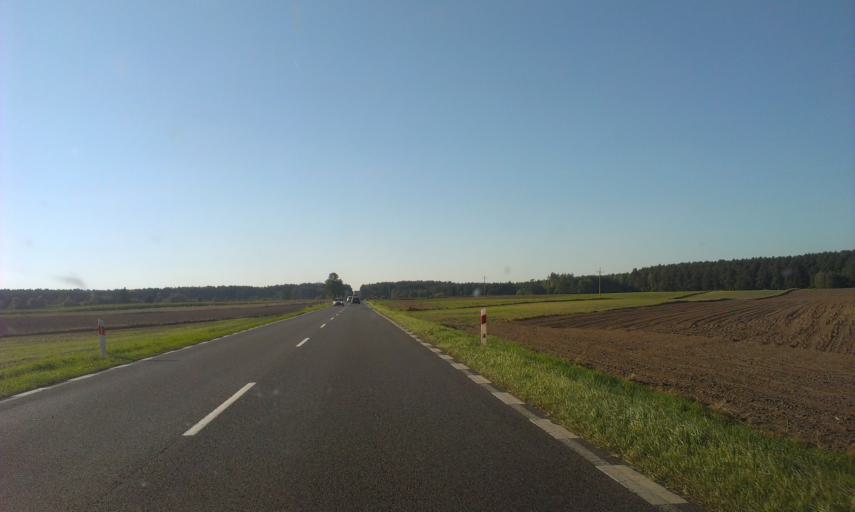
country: PL
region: Kujawsko-Pomorskie
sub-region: Powiat swiecki
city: Swiekatowo
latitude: 53.4770
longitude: 18.1474
